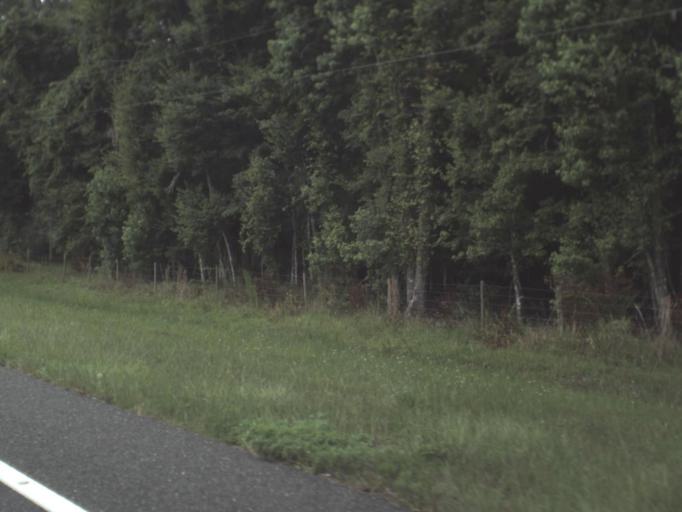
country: US
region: Florida
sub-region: Levy County
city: Chiefland
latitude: 29.4396
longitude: -82.8373
